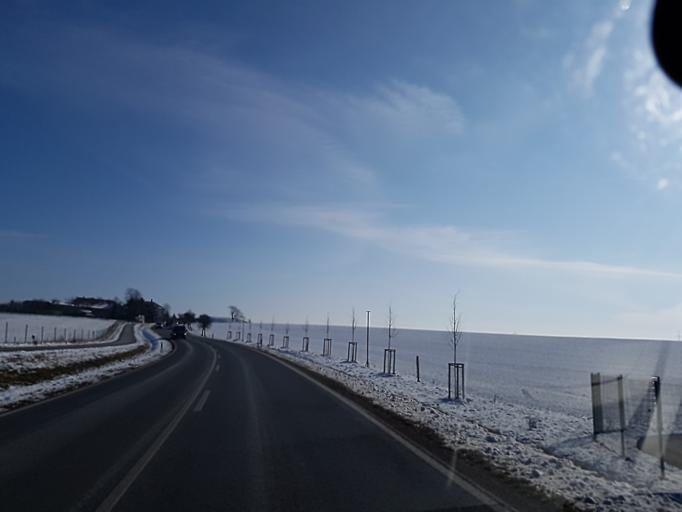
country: DE
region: Saxony
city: Leisnig
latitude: 51.1431
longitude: 12.9430
